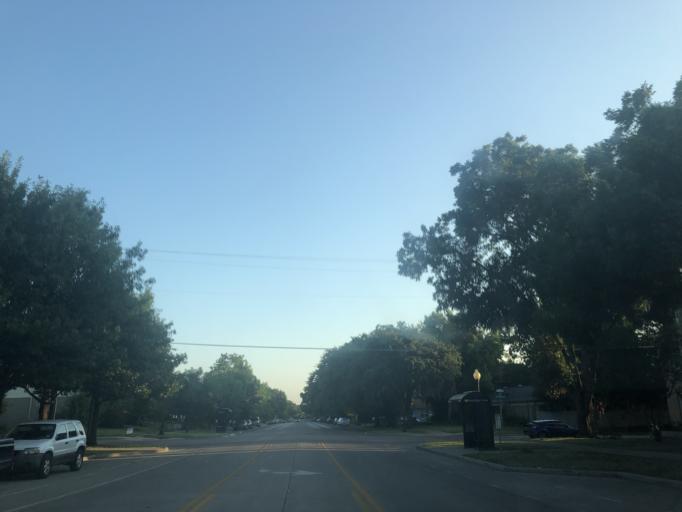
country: US
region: Texas
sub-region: Dallas County
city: Dallas
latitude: 32.7517
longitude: -96.8279
